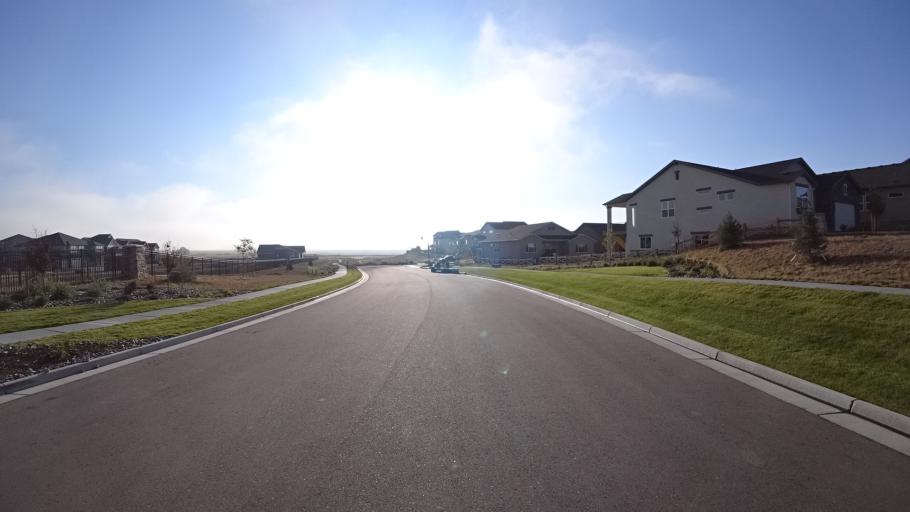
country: US
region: Colorado
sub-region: El Paso County
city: Cimarron Hills
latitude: 38.9314
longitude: -104.6547
